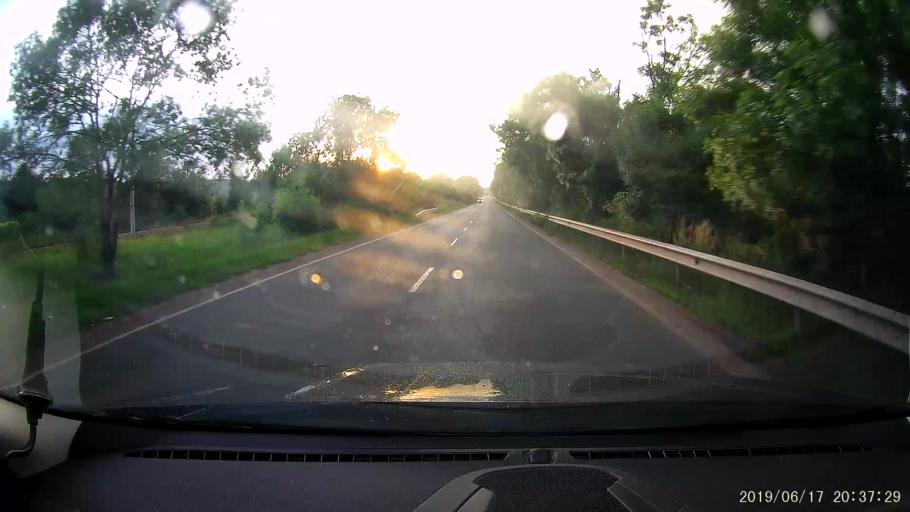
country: BG
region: Sofiya
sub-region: Obshtina Slivnitsa
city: Slivnitsa
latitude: 42.8626
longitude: 23.0316
